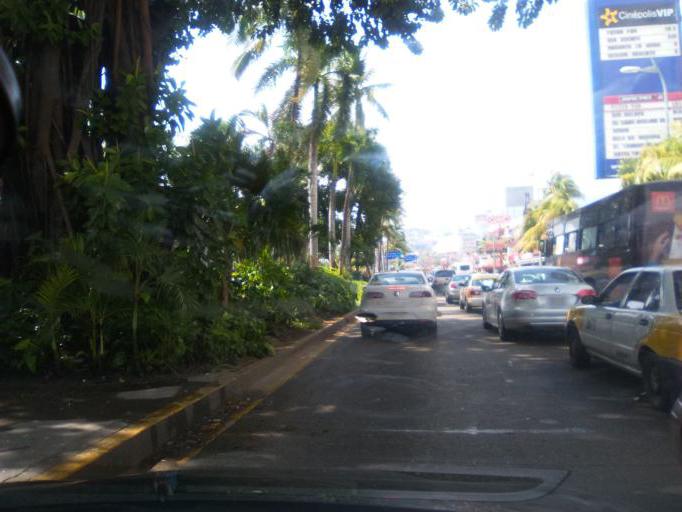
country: MX
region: Guerrero
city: Acapulco de Juarez
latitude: 16.8600
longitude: -99.8736
